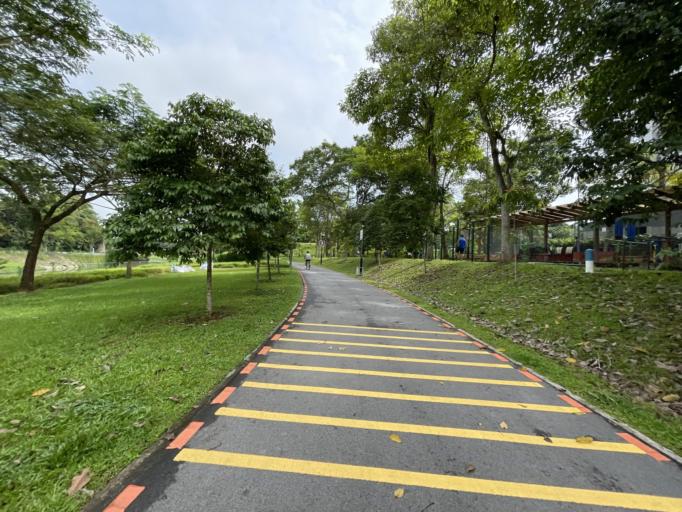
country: SG
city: Singapore
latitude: 1.3222
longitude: 103.7683
